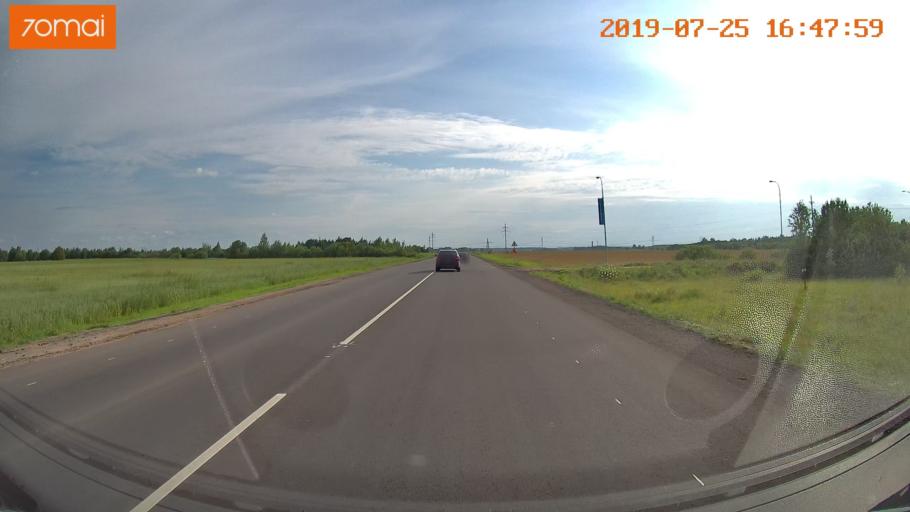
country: RU
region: Ivanovo
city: Privolzhsk
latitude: 57.3614
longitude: 41.2661
